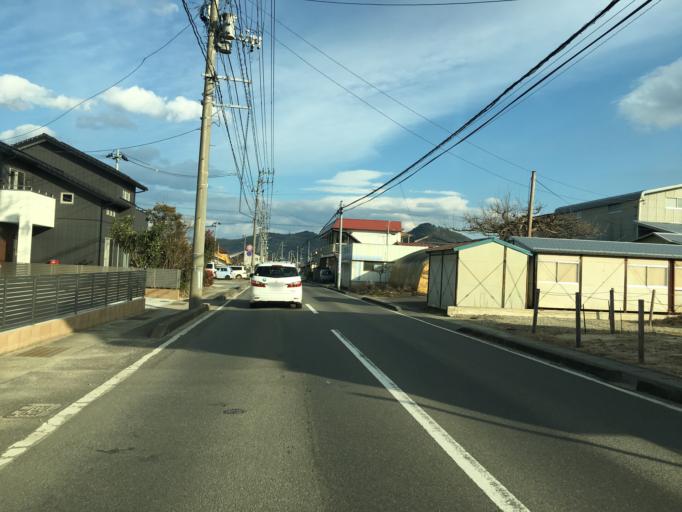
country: JP
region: Fukushima
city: Fukushima-shi
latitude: 37.7766
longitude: 140.4362
